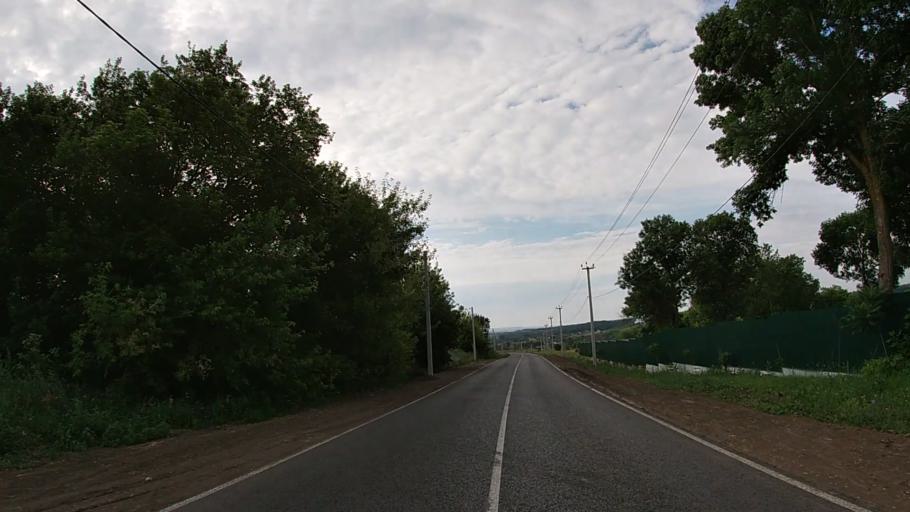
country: RU
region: Belgorod
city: Severnyy
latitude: 50.7184
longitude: 36.5885
